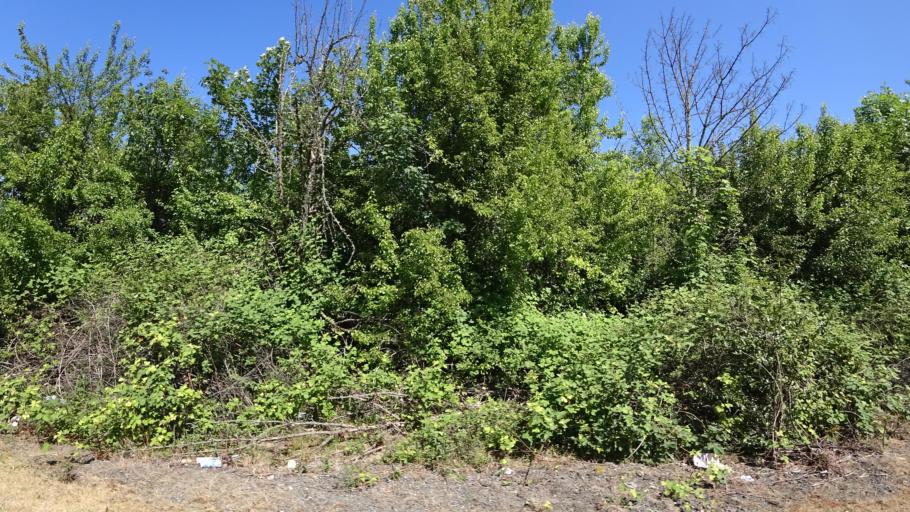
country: US
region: Oregon
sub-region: Clackamas County
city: Happy Valley
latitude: 45.4648
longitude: -122.4858
